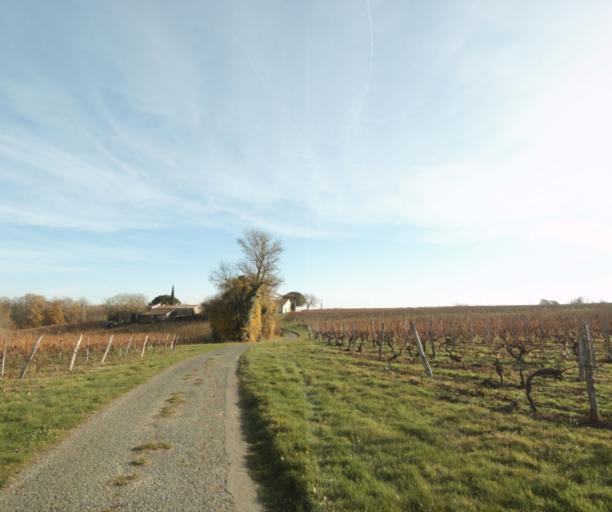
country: FR
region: Poitou-Charentes
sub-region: Departement de la Charente-Maritime
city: Chaniers
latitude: 45.7354
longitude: -0.5179
